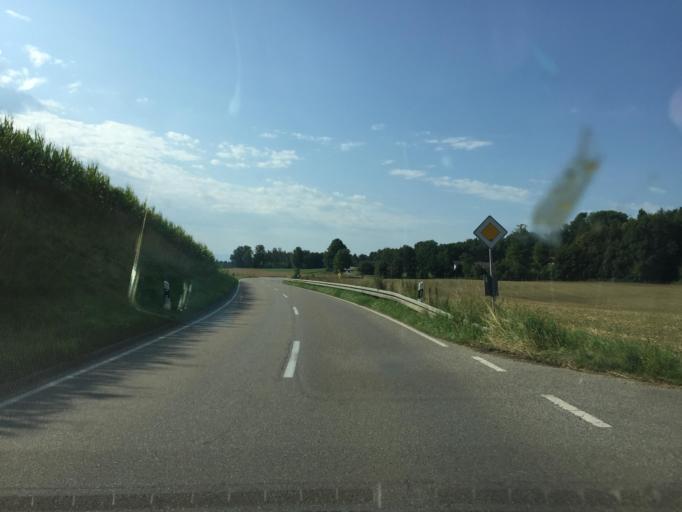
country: DE
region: Bavaria
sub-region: Upper Bavaria
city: Assling
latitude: 47.9842
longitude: 12.0023
